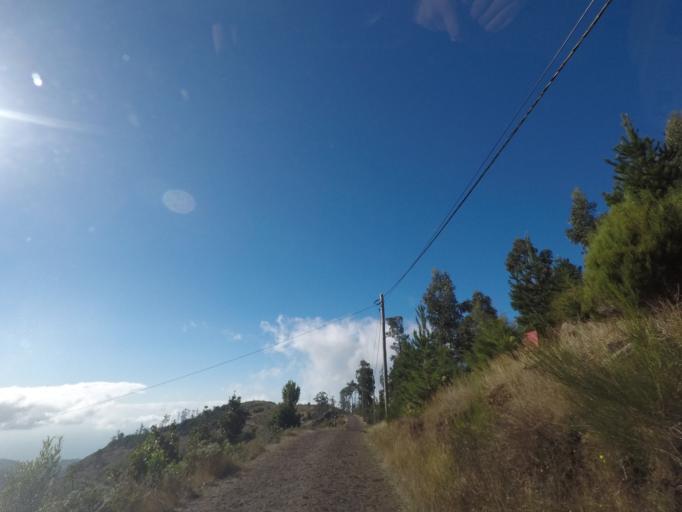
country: PT
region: Madeira
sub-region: Funchal
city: Nossa Senhora do Monte
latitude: 32.6979
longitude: -16.9044
